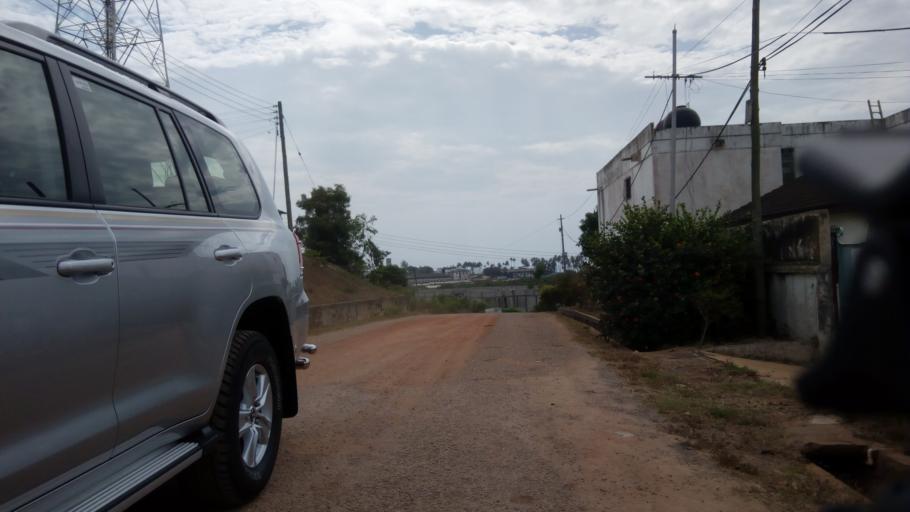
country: GH
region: Central
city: Cape Coast
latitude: 5.1039
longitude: -1.2706
